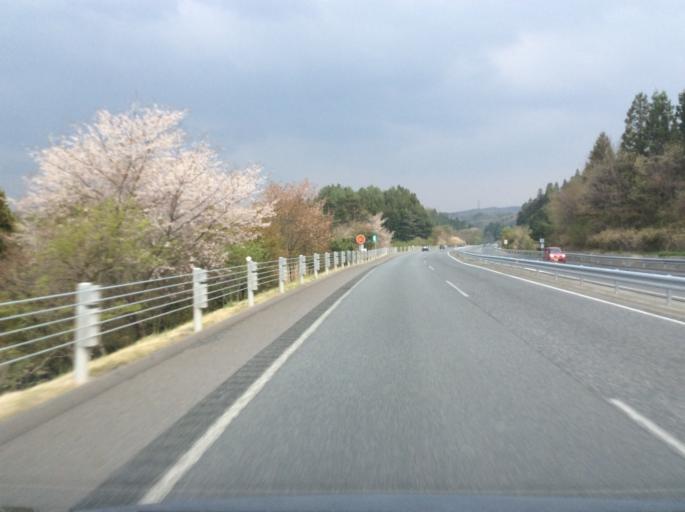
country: JP
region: Fukushima
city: Funehikimachi-funehiki
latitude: 37.2635
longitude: 140.6464
